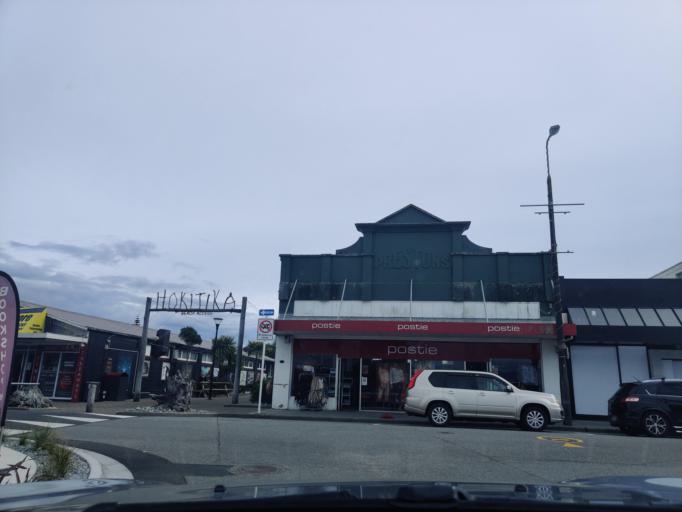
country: NZ
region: West Coast
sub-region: Westland District
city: Hokitika
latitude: -42.7172
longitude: 170.9618
